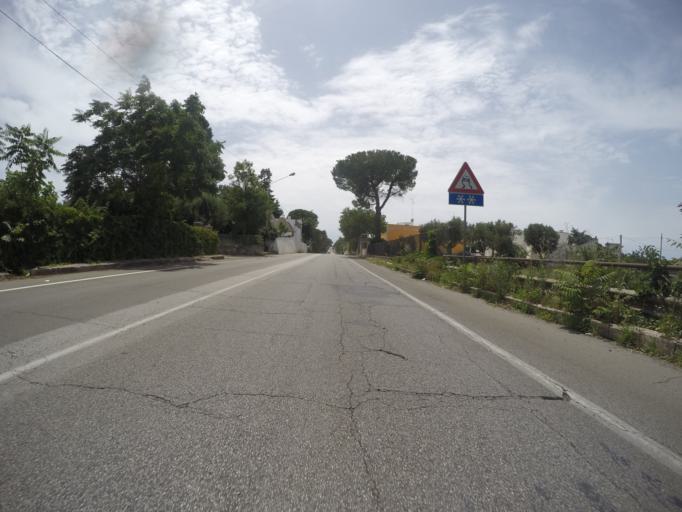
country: IT
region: Apulia
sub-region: Provincia di Taranto
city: Martina Franca
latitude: 40.6936
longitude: 17.3357
